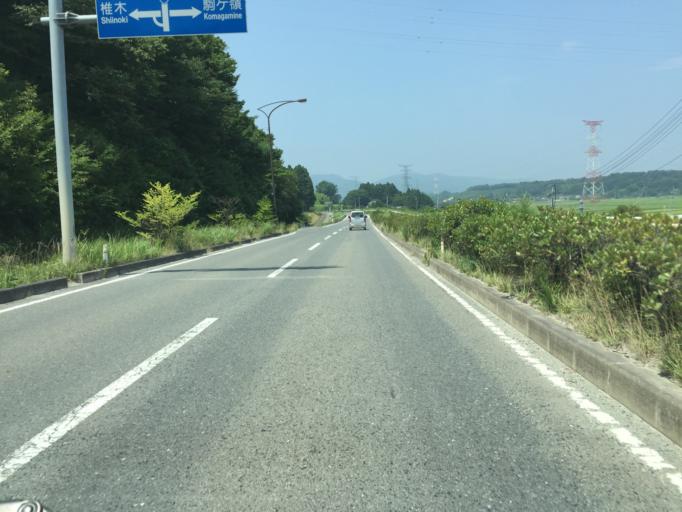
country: JP
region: Miyagi
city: Marumori
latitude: 37.8388
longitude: 140.9136
